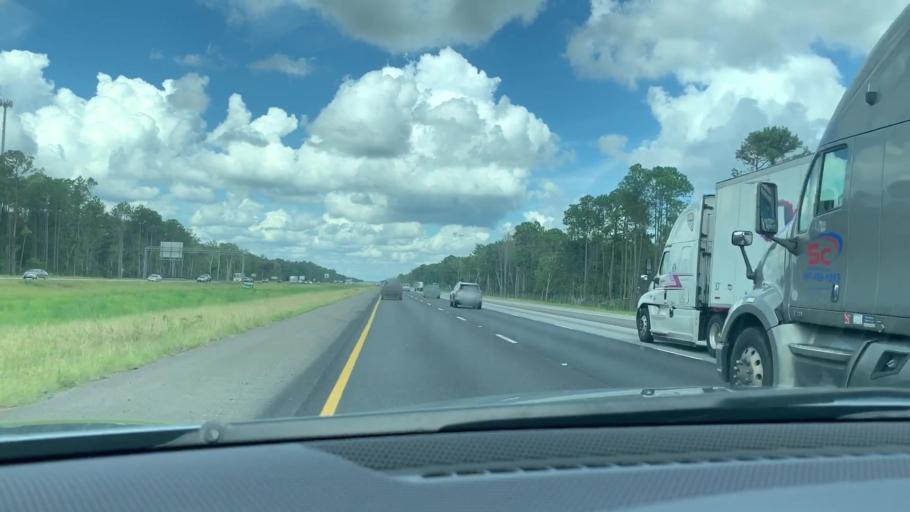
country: US
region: Georgia
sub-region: Camden County
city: Kingsland
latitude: 30.7951
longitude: -81.6596
